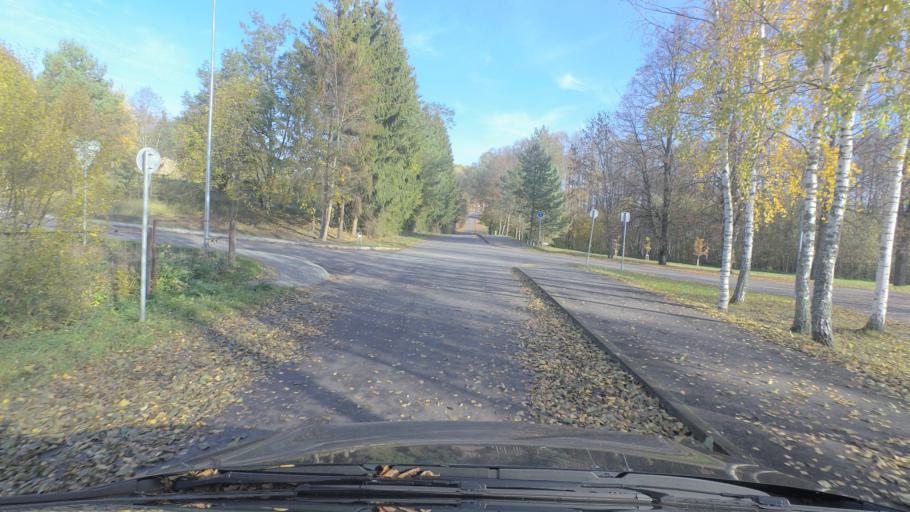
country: LT
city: Ignalina
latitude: 55.3372
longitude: 26.1481
